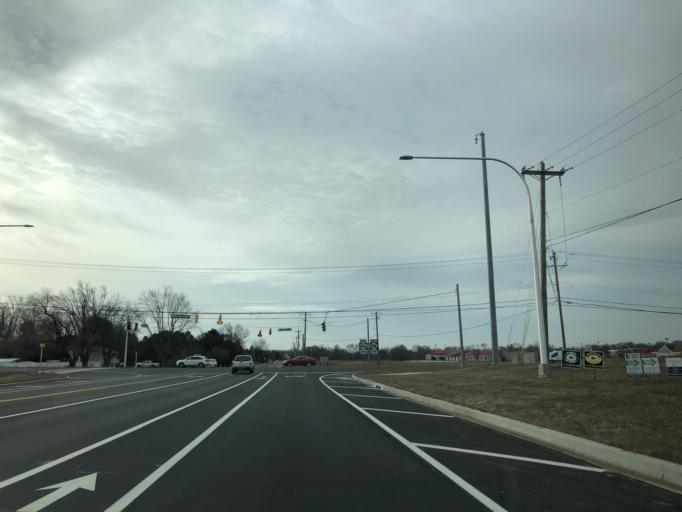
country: US
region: Delaware
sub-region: New Castle County
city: Middletown
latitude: 39.5047
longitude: -75.6841
